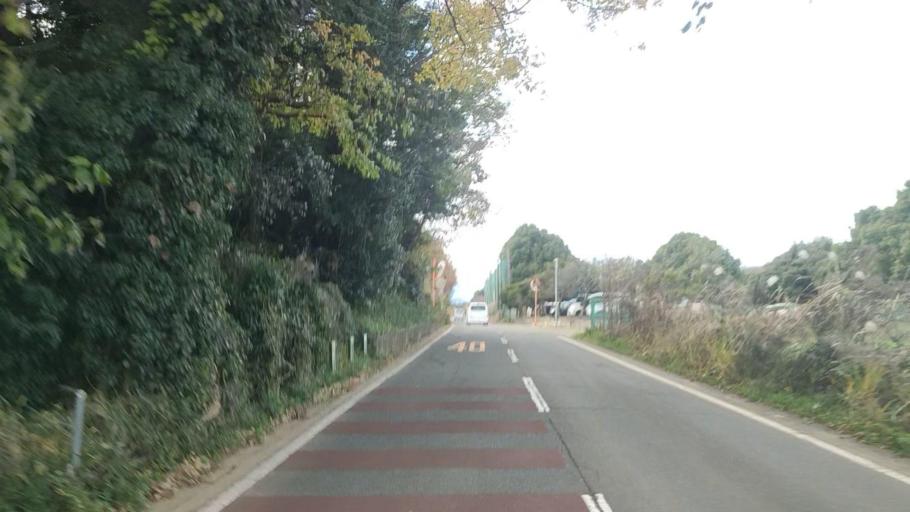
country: JP
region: Kanagawa
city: Minami-rinkan
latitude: 35.4843
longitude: 139.4846
